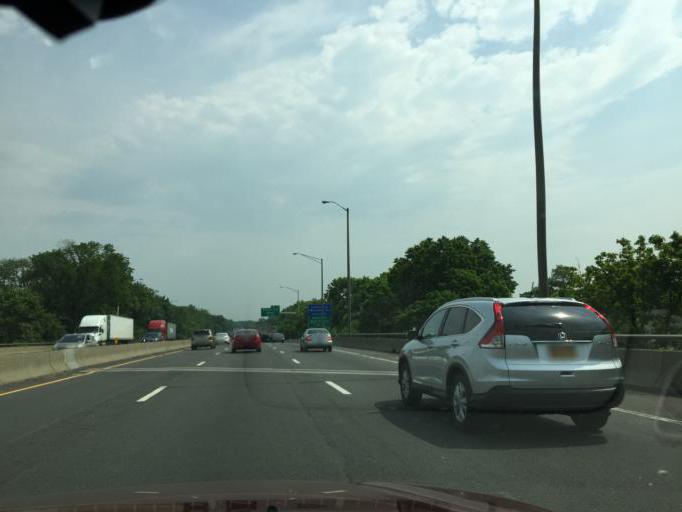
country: US
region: New York
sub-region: Westchester County
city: Port Chester
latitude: 40.9947
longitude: -73.6591
